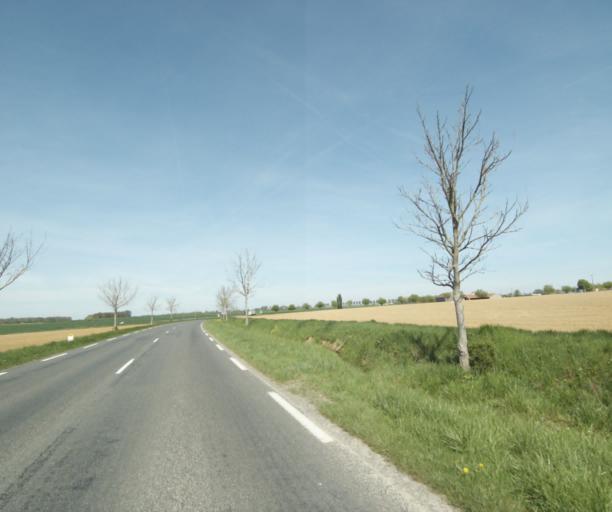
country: FR
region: Ile-de-France
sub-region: Departement de Seine-et-Marne
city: Nangis
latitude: 48.5532
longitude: 2.9977
